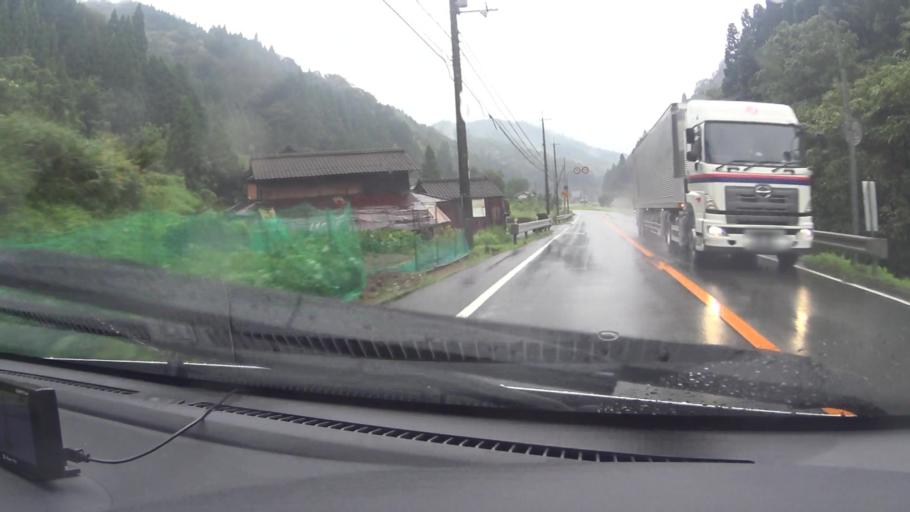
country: JP
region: Kyoto
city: Ayabe
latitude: 35.2345
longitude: 135.3311
